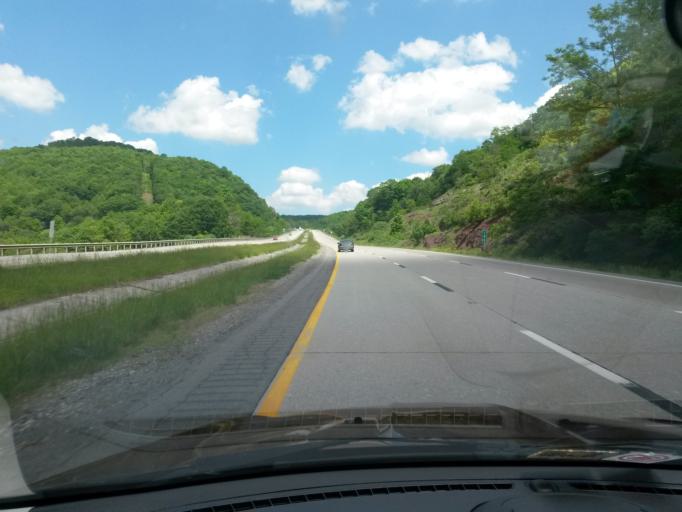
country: US
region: West Virginia
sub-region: Greenbrier County
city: Rainelle
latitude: 37.8305
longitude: -80.7841
